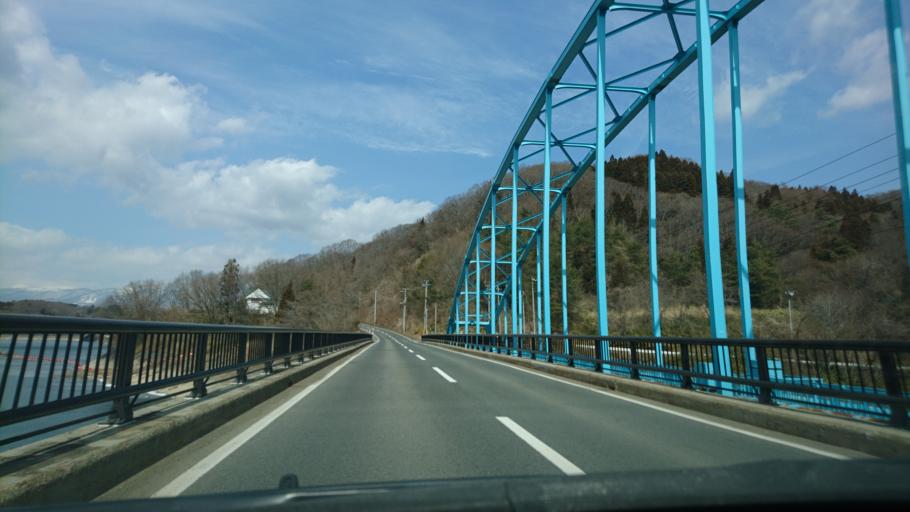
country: JP
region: Iwate
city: Shizukuishi
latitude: 39.6879
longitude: 141.0332
